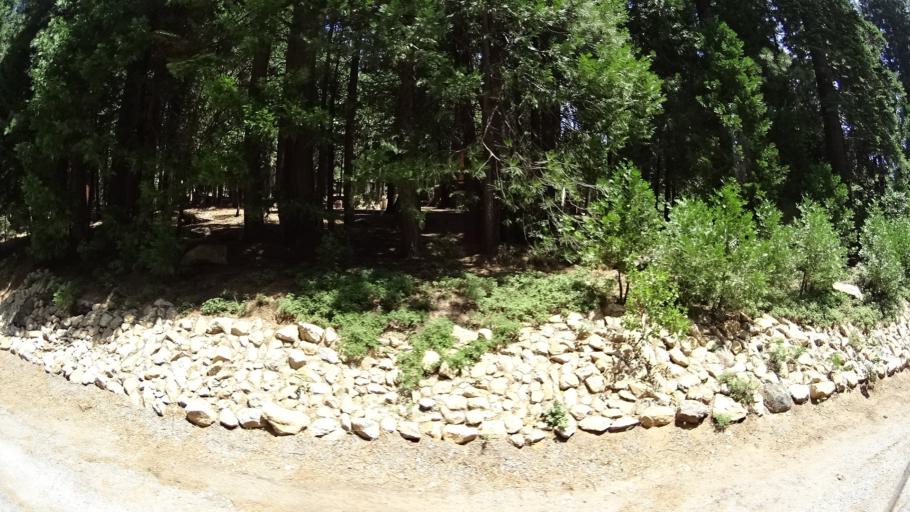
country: US
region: California
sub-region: Calaveras County
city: Arnold
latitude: 38.3018
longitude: -120.2698
